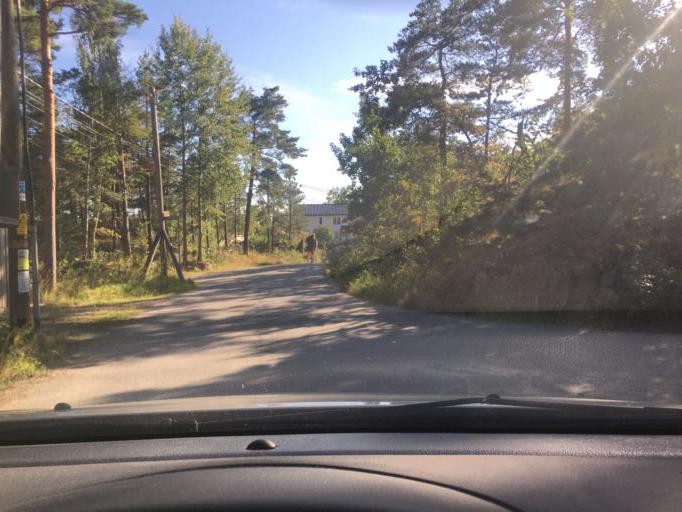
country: SE
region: Stockholm
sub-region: Lidingo
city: Brevik
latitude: 59.3213
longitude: 18.2367
